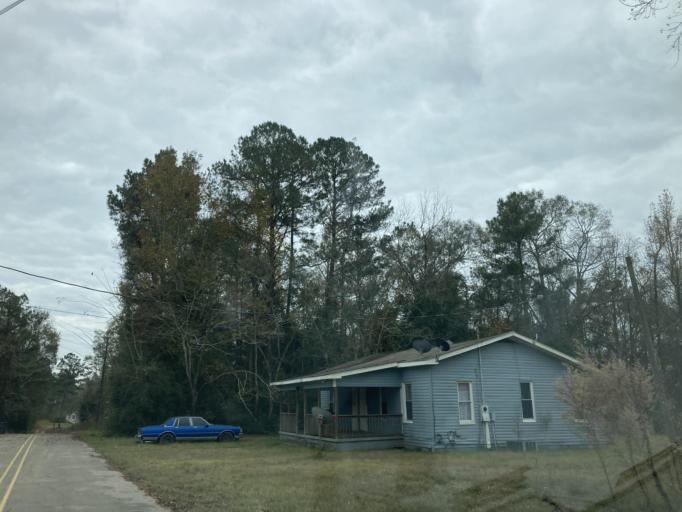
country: US
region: Mississippi
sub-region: Forrest County
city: Hattiesburg
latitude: 31.1655
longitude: -89.2160
